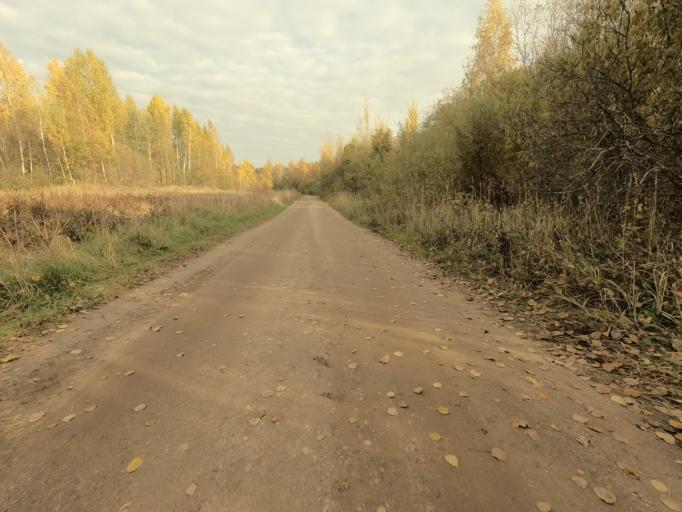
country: RU
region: Novgorod
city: Volkhovskiy
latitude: 58.8930
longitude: 31.0238
